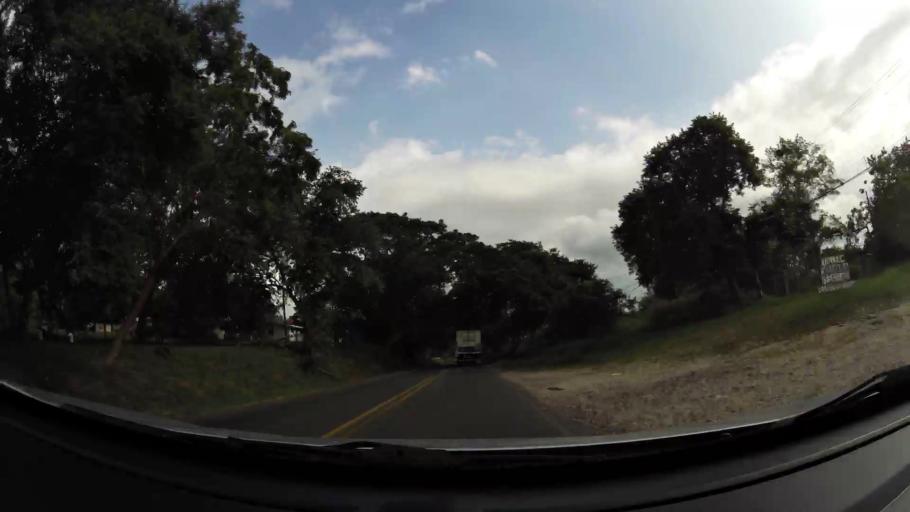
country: CR
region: Guanacaste
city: Juntas
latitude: 10.1839
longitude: -84.9393
